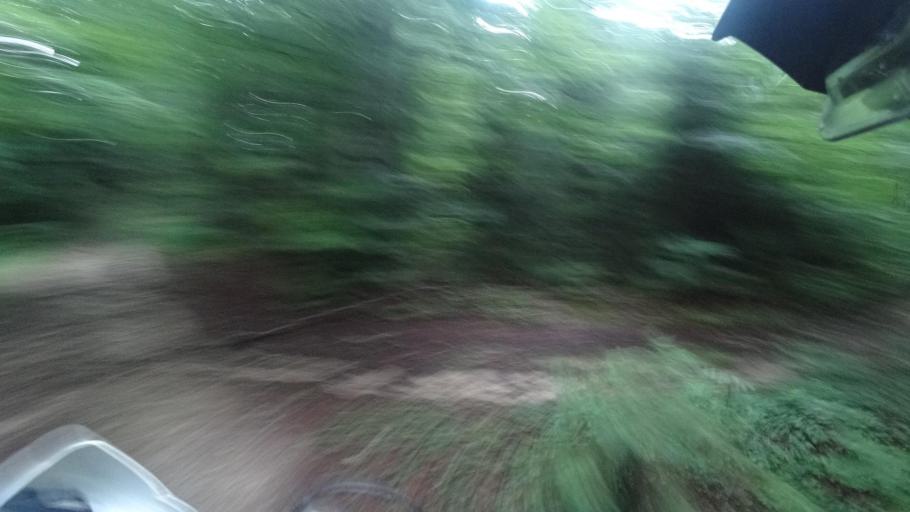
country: HR
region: Licko-Senjska
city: Jezerce
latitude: 44.8210
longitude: 15.6183
